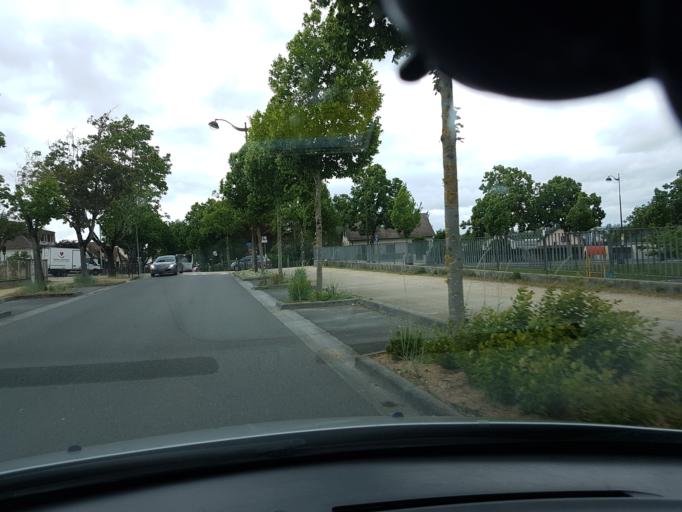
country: FR
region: Centre
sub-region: Departement du Cher
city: Bourges
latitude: 47.1099
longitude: 2.4169
